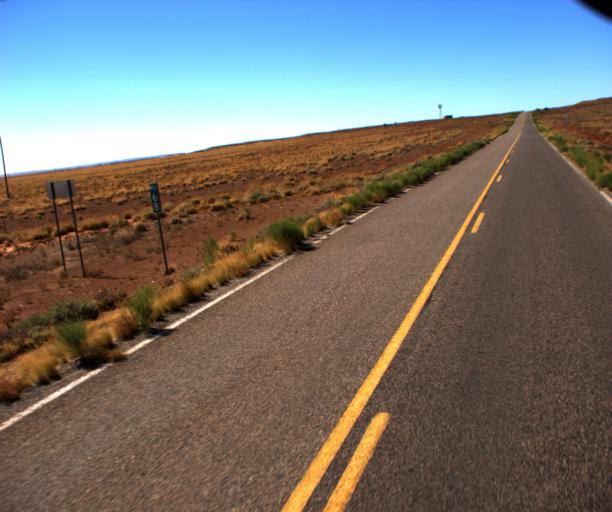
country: US
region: Arizona
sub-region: Coconino County
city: LeChee
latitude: 35.2468
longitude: -110.9610
